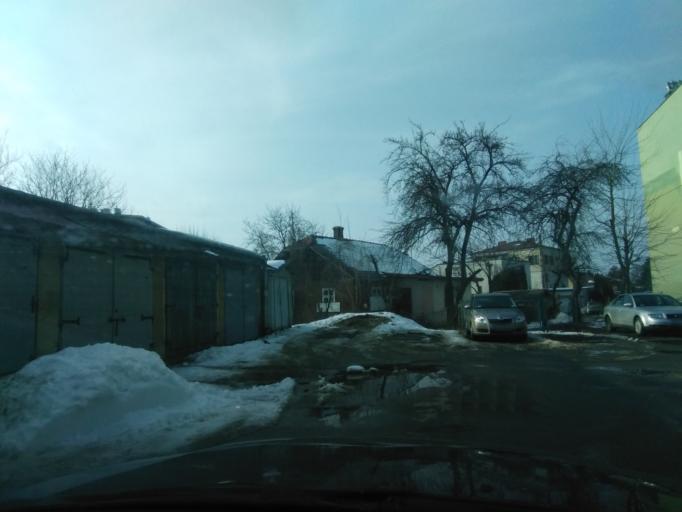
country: PL
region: Subcarpathian Voivodeship
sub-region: Krosno
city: Krosno
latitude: 49.6997
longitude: 21.7471
